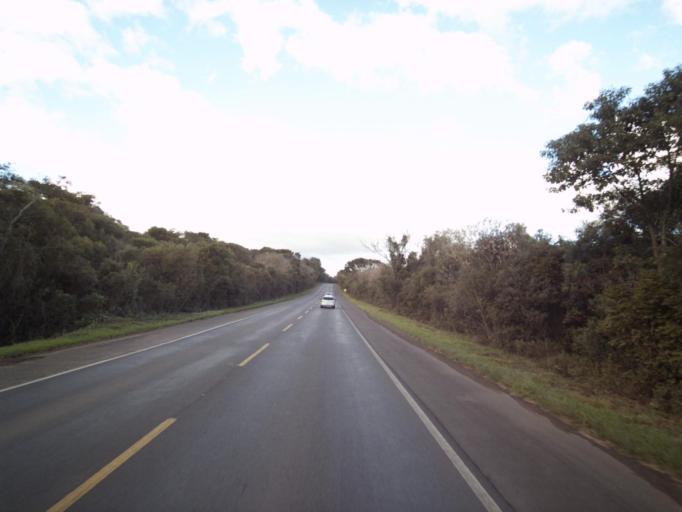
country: BR
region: Santa Catarina
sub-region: Joacaba
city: Joacaba
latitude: -27.3028
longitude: -51.3882
